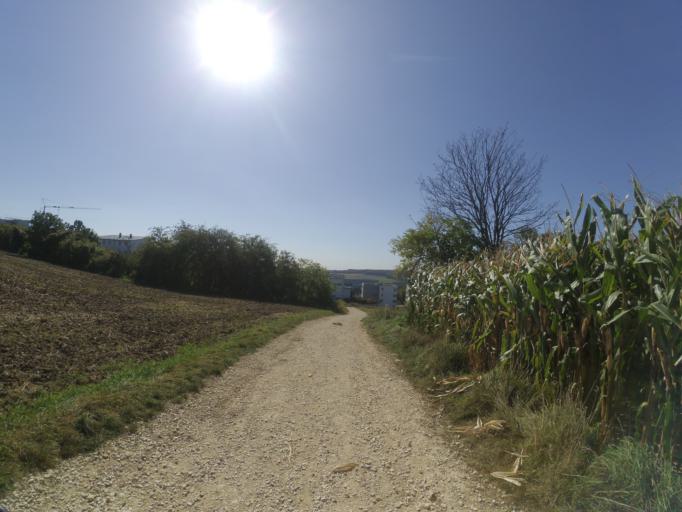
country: DE
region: Baden-Wuerttemberg
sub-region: Tuebingen Region
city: Dornstadt
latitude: 48.4167
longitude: 9.9379
